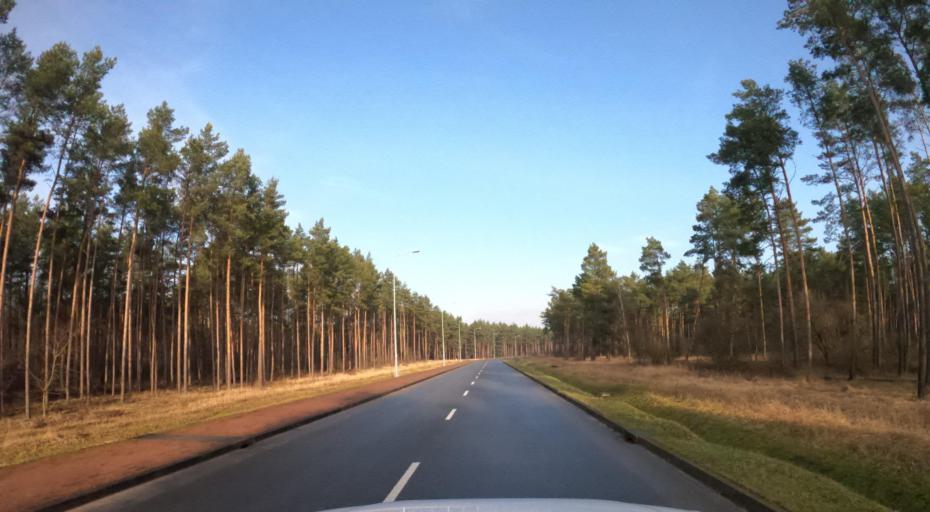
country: PL
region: Lubusz
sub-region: Powiat gorzowski
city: Kostrzyn nad Odra
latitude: 52.6224
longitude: 14.6072
